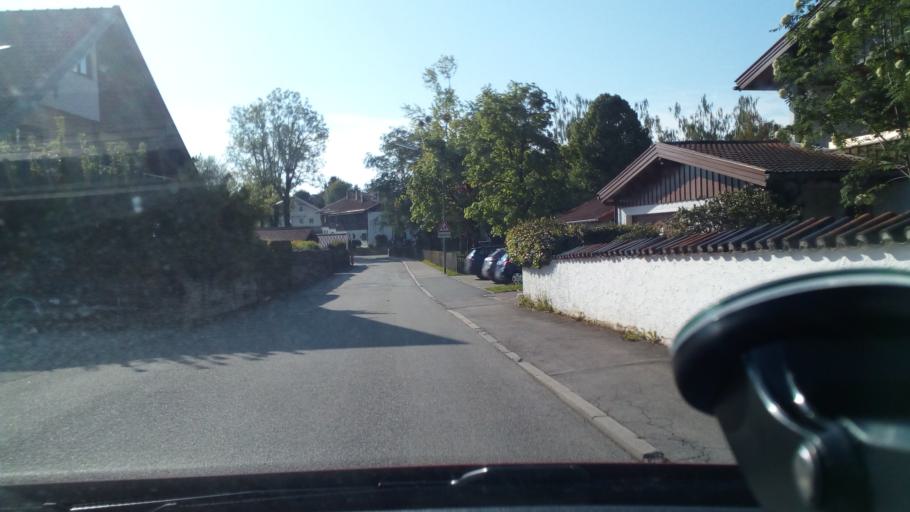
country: DE
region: Bavaria
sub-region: Upper Bavaria
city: Holzkirchen
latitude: 47.8782
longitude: 11.6942
